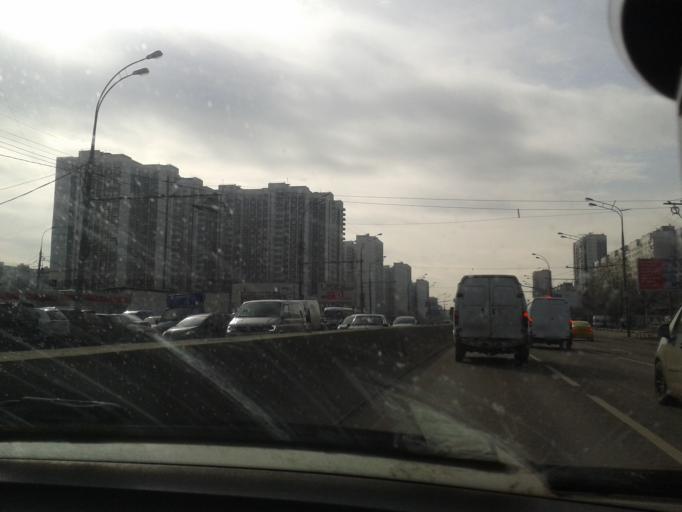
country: RU
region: Moscow
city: Lianozovo
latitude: 55.8999
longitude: 37.5869
